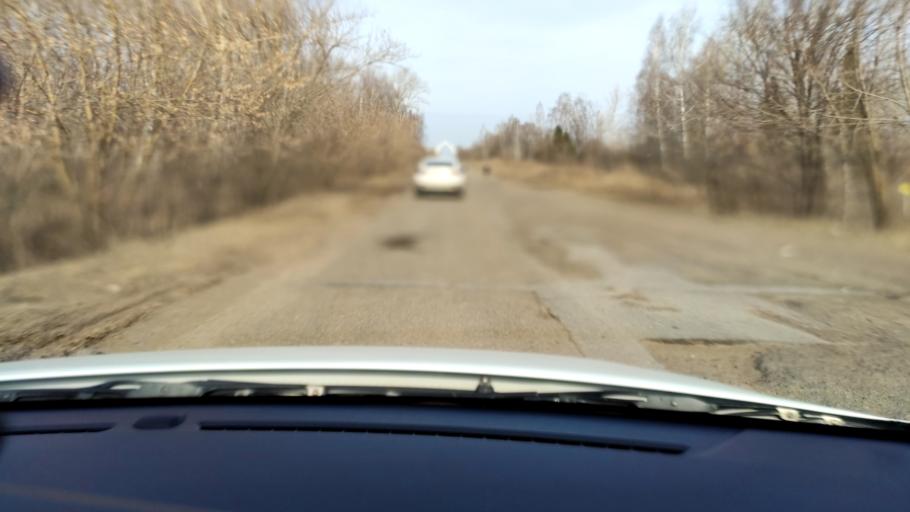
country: RU
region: Tatarstan
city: Stolbishchi
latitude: 55.7211
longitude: 49.2096
